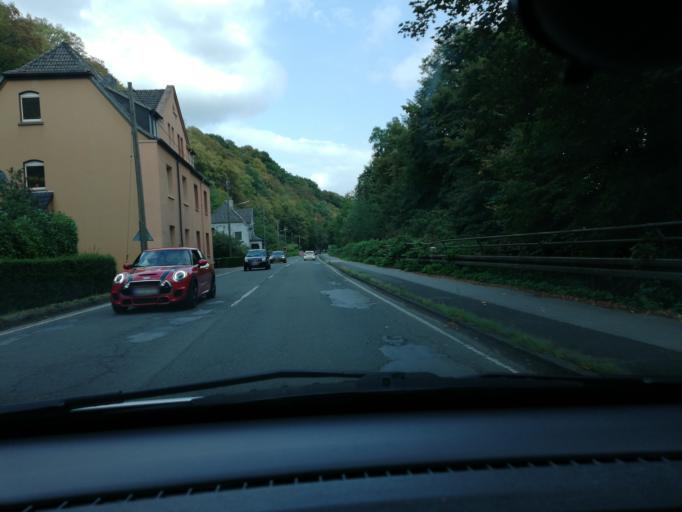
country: DE
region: North Rhine-Westphalia
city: Witten
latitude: 51.4339
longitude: 7.3070
